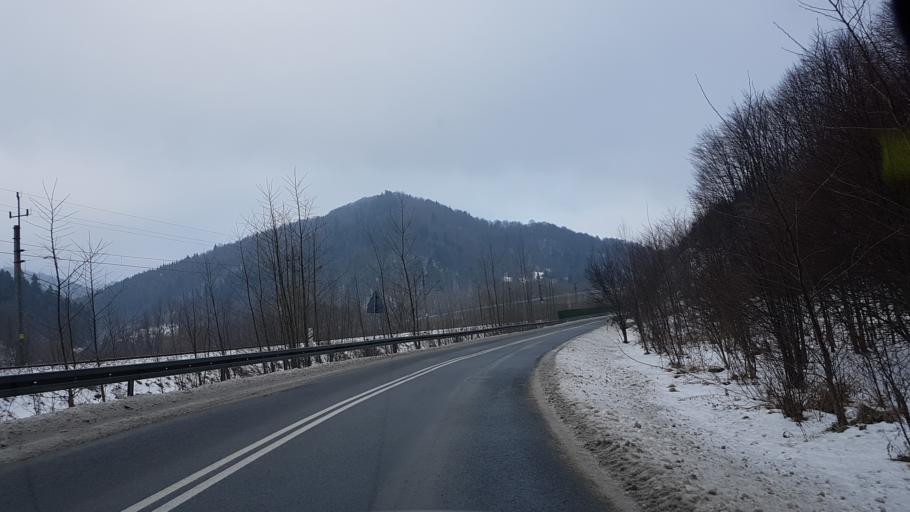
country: PL
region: Lesser Poland Voivodeship
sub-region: Powiat nowosadecki
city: Piwniczna-Zdroj
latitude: 49.4163
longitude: 20.7287
